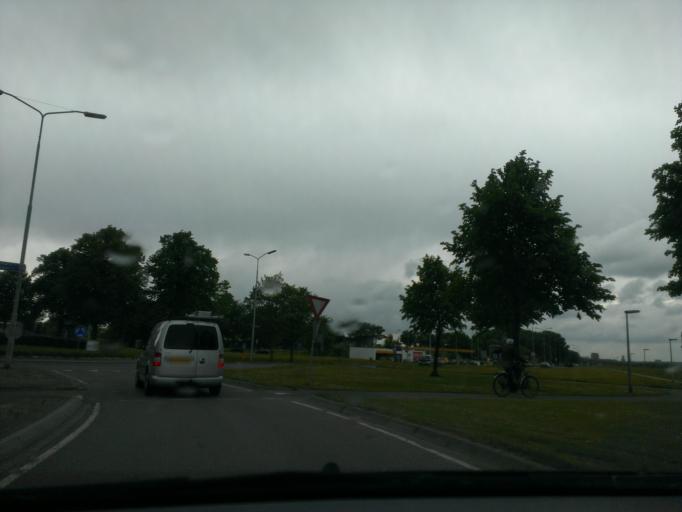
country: NL
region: Gelderland
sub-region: Gemeente Westervoort
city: Westervoort
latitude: 51.9412
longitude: 5.9410
